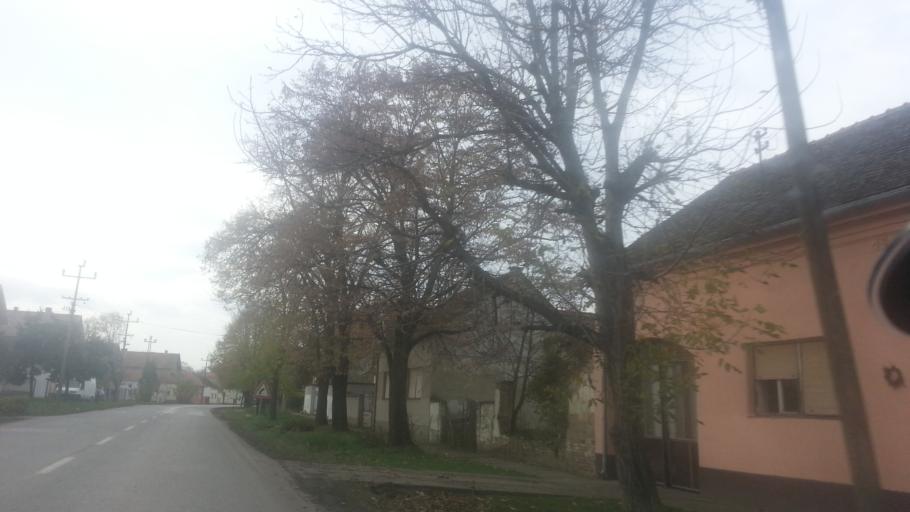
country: RS
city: Putinci
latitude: 44.9916
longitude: 19.9786
